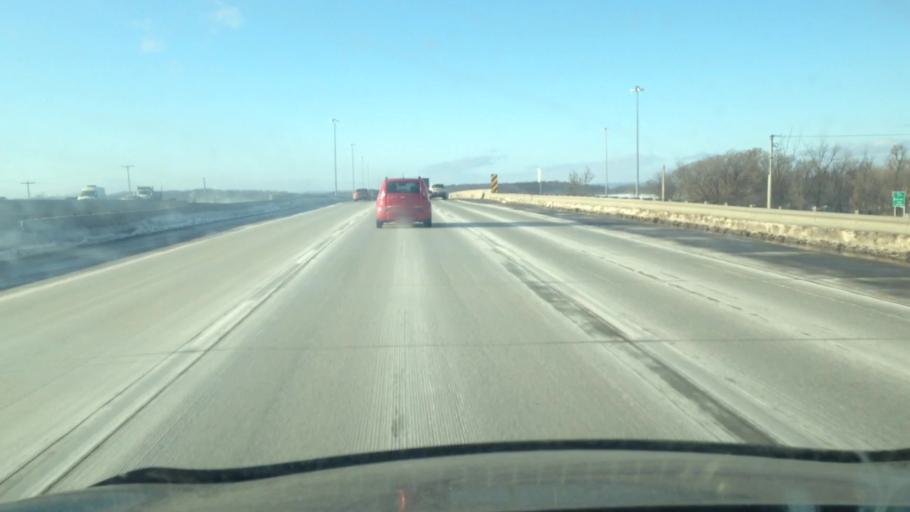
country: CA
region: Quebec
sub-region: Laurentides
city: Blainville
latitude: 45.6921
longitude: -73.9360
